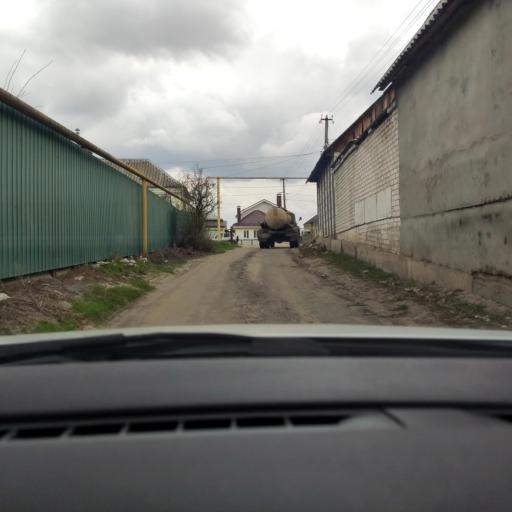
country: RU
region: Voronezj
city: Pridonskoy
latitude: 51.7104
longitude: 39.0731
